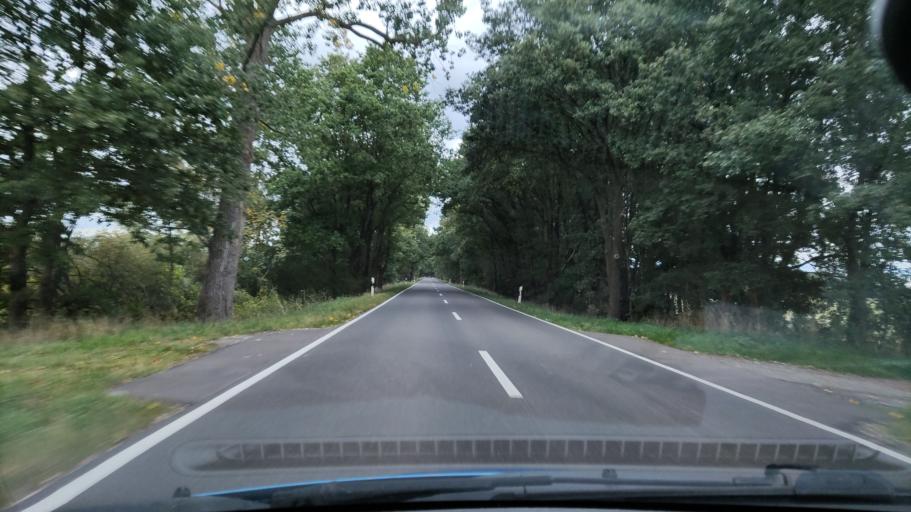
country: DE
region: Lower Saxony
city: Neu Darchau
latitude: 53.3403
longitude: 10.9514
